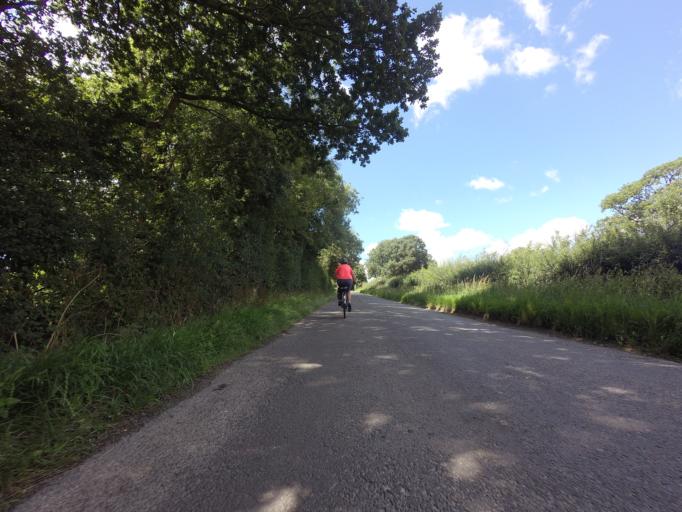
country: GB
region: England
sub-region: East Sussex
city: Horam
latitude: 50.8969
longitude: 0.1919
